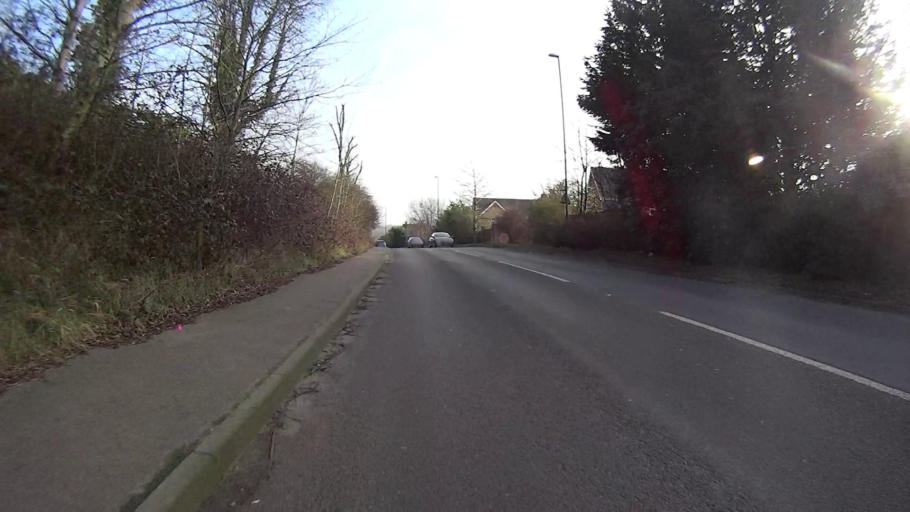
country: GB
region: England
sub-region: West Sussex
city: Maidenbower
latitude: 51.1115
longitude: -0.1470
